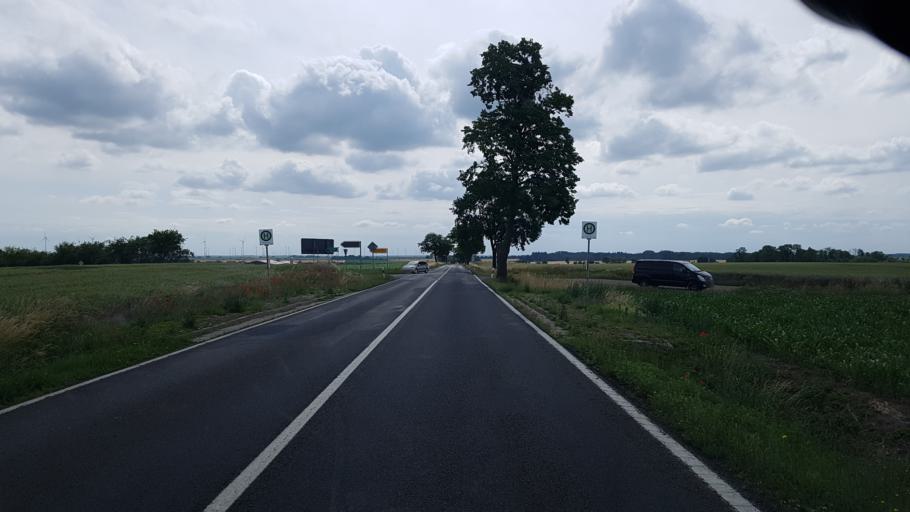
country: DE
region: Mecklenburg-Vorpommern
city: Strasburg
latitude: 53.4052
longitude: 13.7426
